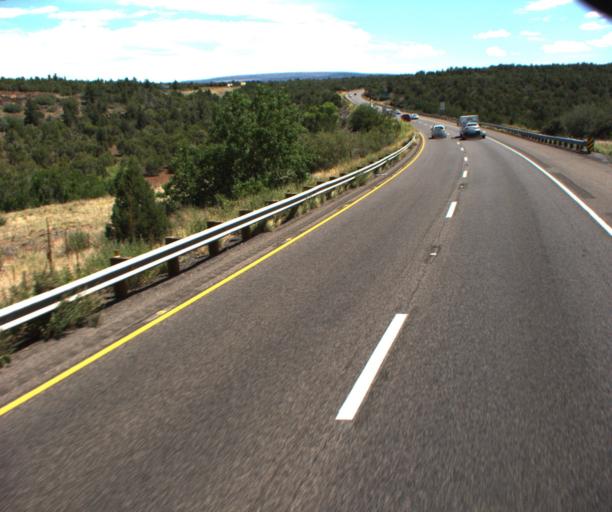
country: US
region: Arizona
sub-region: Yavapai County
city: Village of Oak Creek (Big Park)
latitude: 34.7690
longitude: -111.6412
